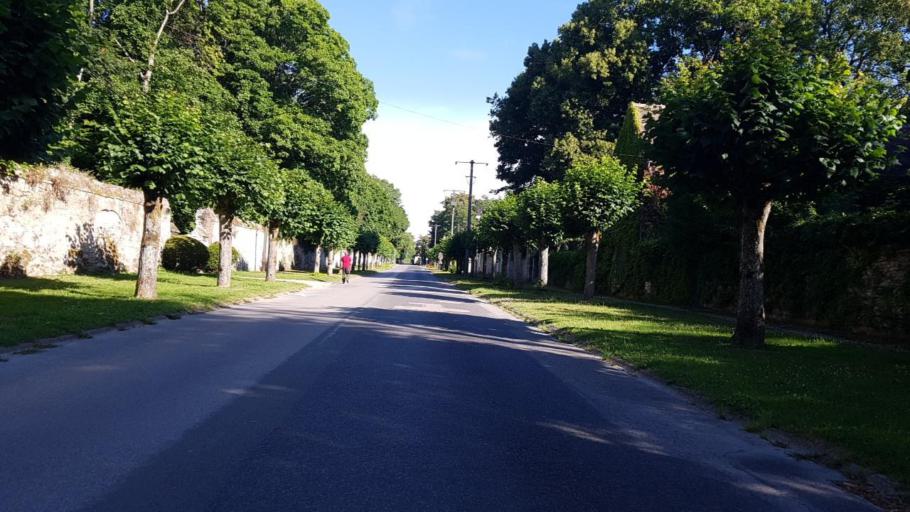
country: FR
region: Picardie
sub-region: Departement de l'Oise
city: Chamant
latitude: 49.2245
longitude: 2.6069
